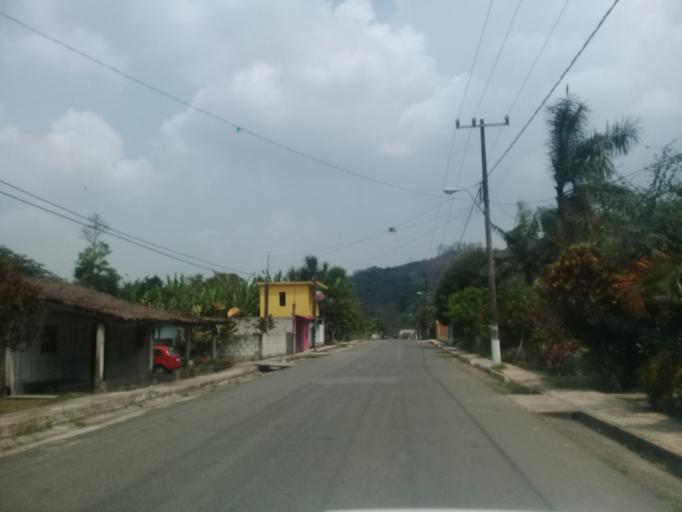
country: MX
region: Veracruz
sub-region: Cordoba
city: San Jose de Tapia
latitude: 18.8236
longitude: -96.9797
